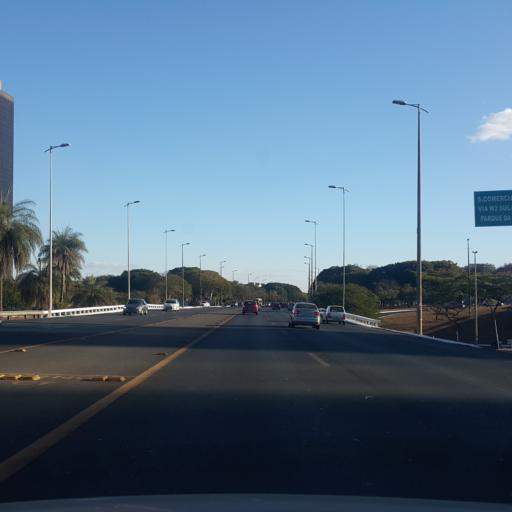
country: BR
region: Federal District
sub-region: Brasilia
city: Brasilia
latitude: -15.7999
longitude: -47.8851
